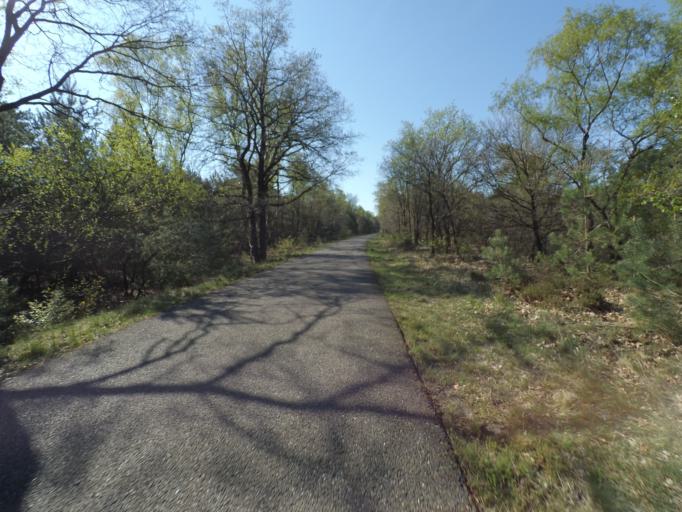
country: NL
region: Gelderland
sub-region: Gemeente Ede
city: Harskamp
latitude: 52.1820
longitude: 5.8146
